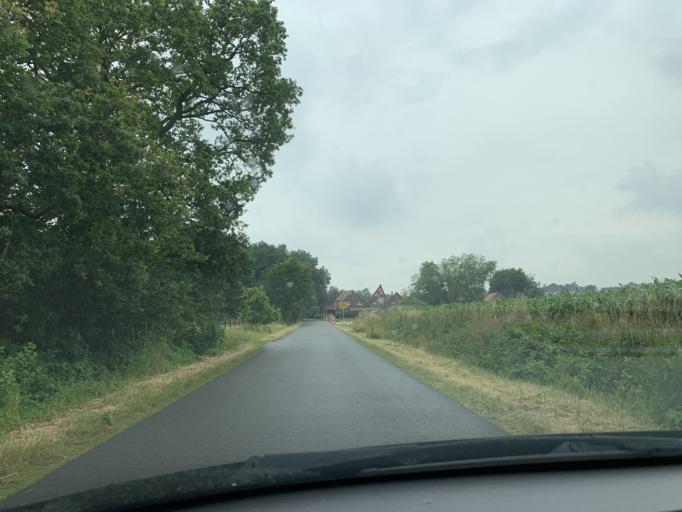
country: DE
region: Lower Saxony
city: Westerstede
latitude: 53.2585
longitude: 7.9065
